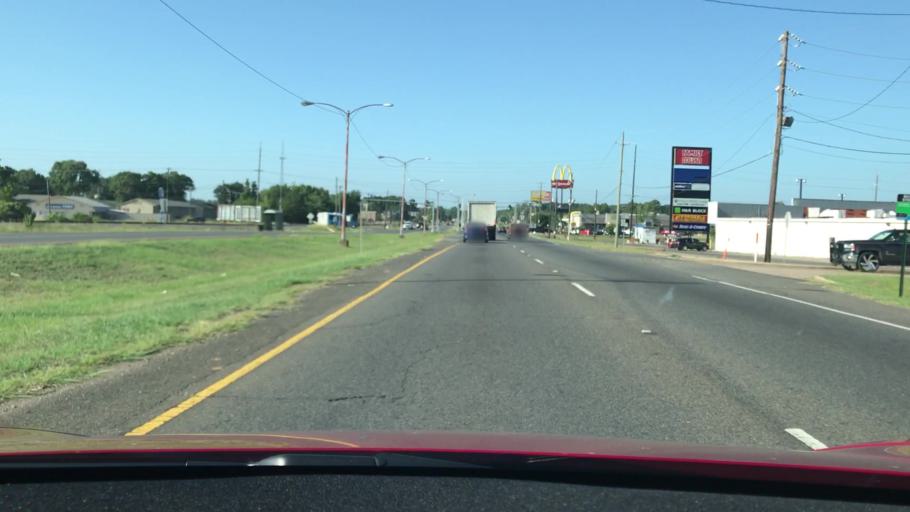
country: US
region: Louisiana
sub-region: Caddo Parish
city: Shreveport
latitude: 32.4438
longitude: -93.7807
